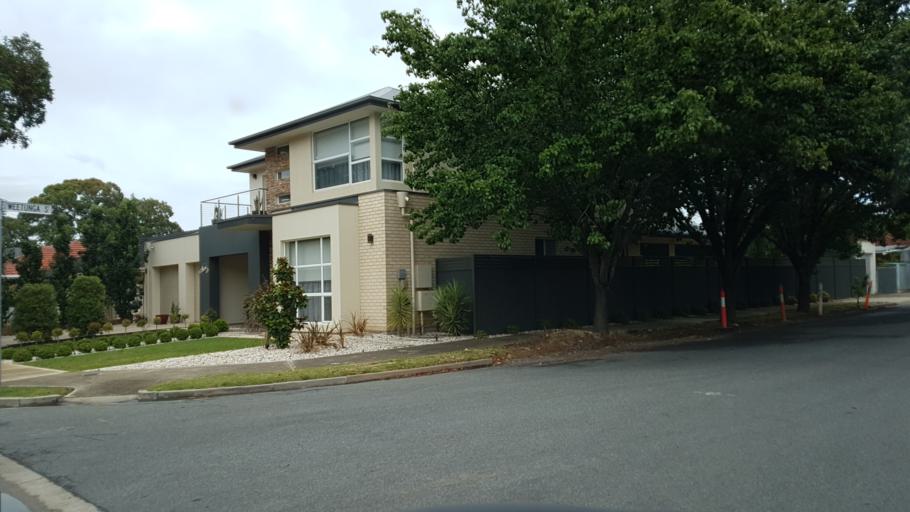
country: AU
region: South Australia
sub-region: Charles Sturt
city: Seaton
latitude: -34.9246
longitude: 138.5206
